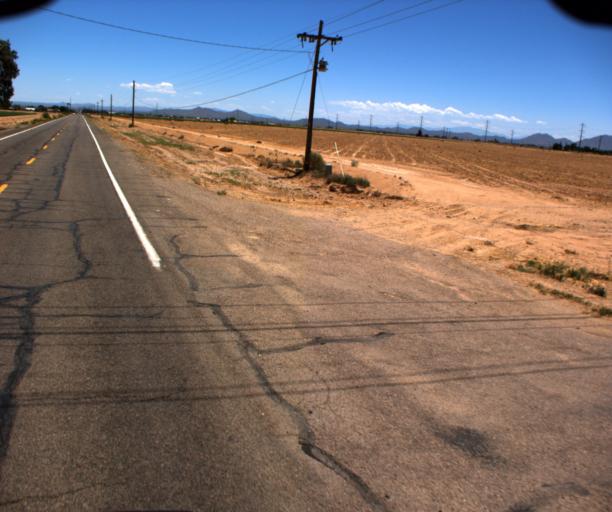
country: US
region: Arizona
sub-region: Pinal County
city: Coolidge
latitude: 32.8795
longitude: -111.5324
